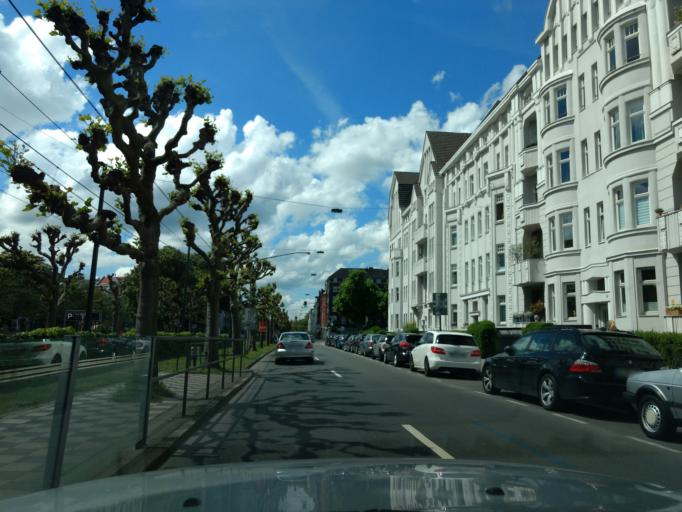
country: DE
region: North Rhine-Westphalia
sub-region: Regierungsbezirk Dusseldorf
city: Dusseldorf
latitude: 51.2316
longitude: 6.7541
